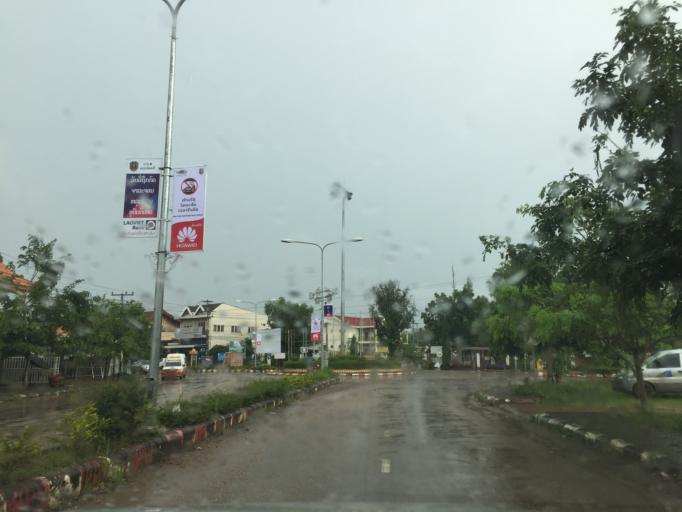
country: LA
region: Attapu
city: Attapu
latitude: 14.8210
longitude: 106.8124
